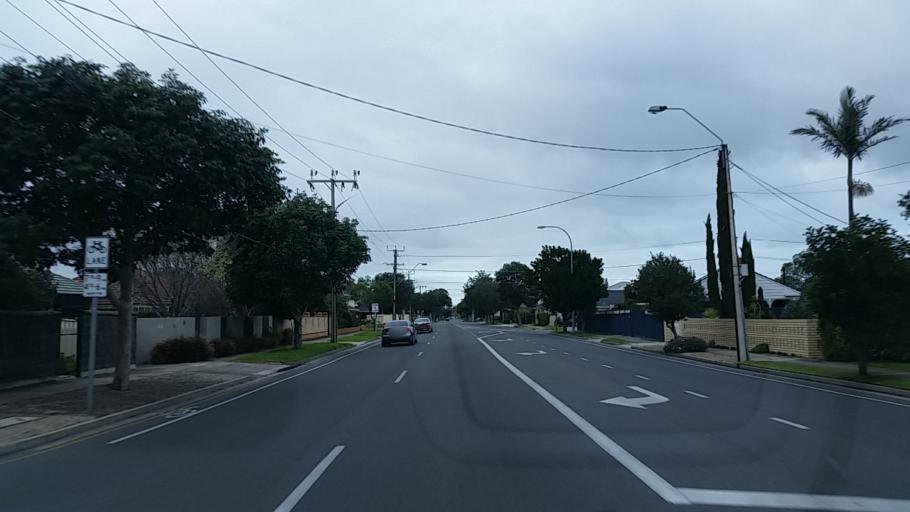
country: AU
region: South Australia
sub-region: Charles Sturt
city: Findon
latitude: -34.9196
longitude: 138.5353
